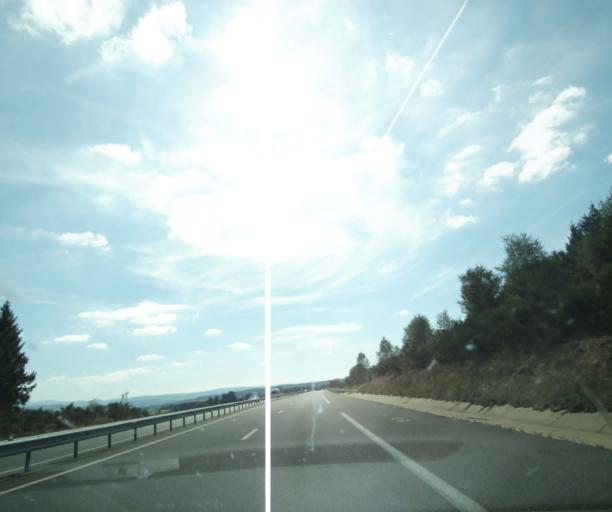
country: FR
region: Auvergne
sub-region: Departement du Puy-de-Dome
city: Gelles
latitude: 45.7041
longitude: 2.6959
